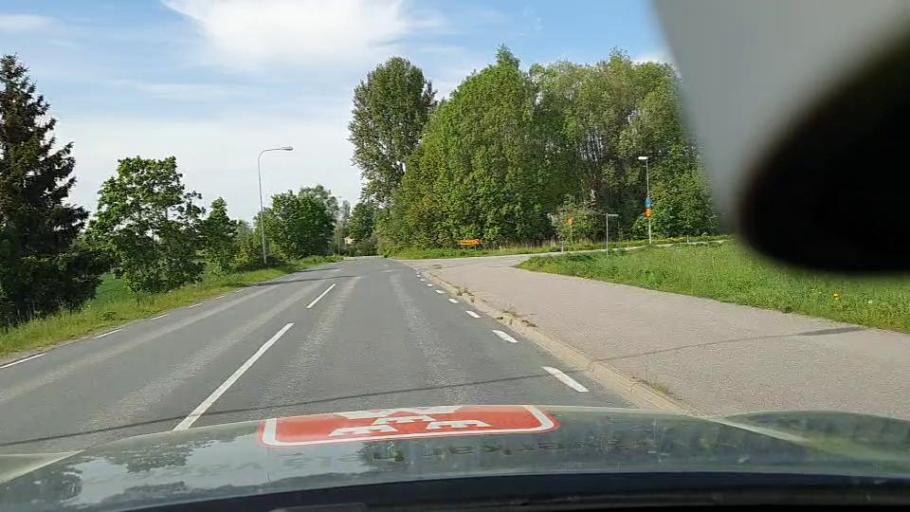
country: SE
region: Soedermanland
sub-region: Eskilstuna Kommun
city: Arla
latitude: 59.2789
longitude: 16.6702
